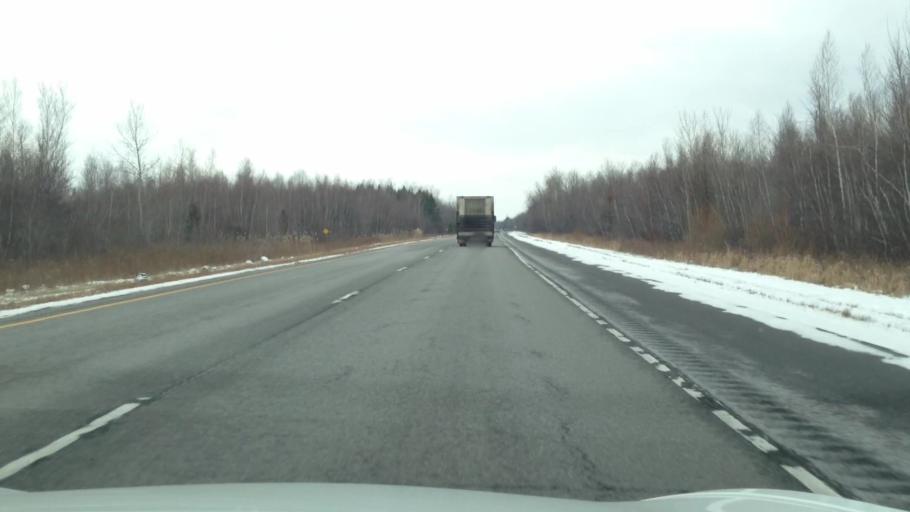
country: CA
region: Ontario
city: Casselman
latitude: 45.3164
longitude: -75.1801
